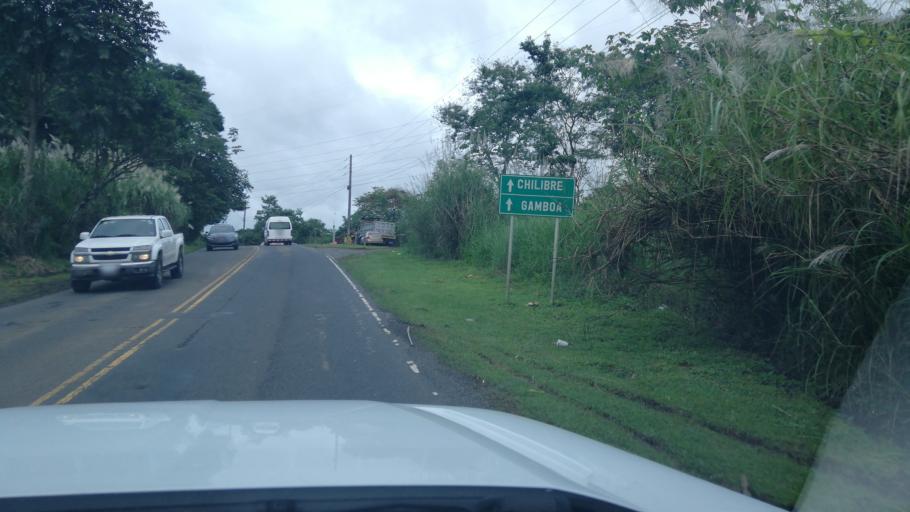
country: PA
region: Panama
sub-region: Distrito de Panama
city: Paraiso
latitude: 9.0386
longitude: -79.6322
